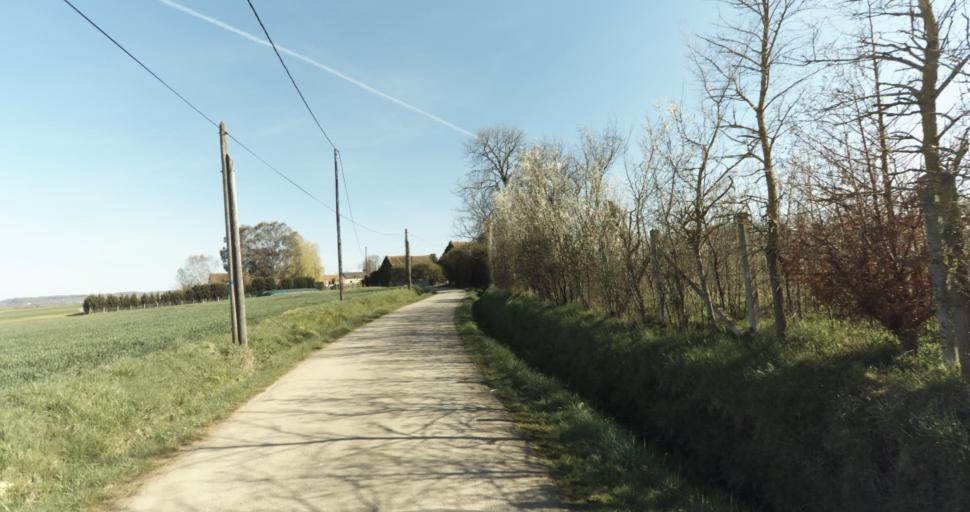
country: FR
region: Lower Normandy
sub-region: Departement du Calvados
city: Saint-Pierre-sur-Dives
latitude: 49.0383
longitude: -0.0090
